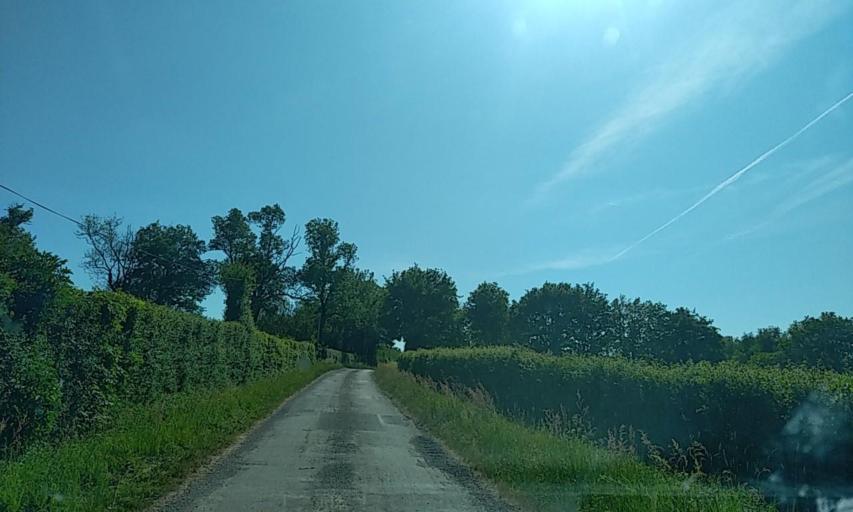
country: FR
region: Poitou-Charentes
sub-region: Departement des Deux-Sevres
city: Boisme
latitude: 46.7722
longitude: -0.4052
